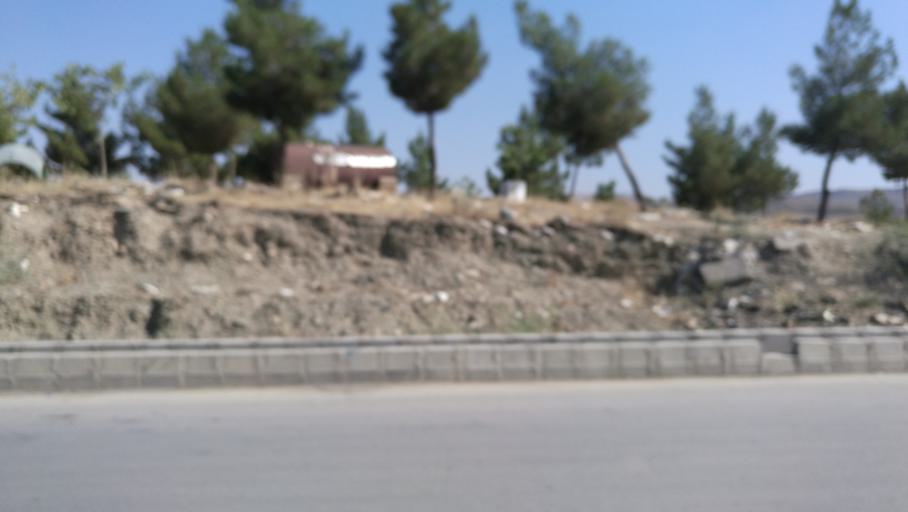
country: IR
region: Razavi Khorasan
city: Torqabeh
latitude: 36.3910
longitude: 59.2726
